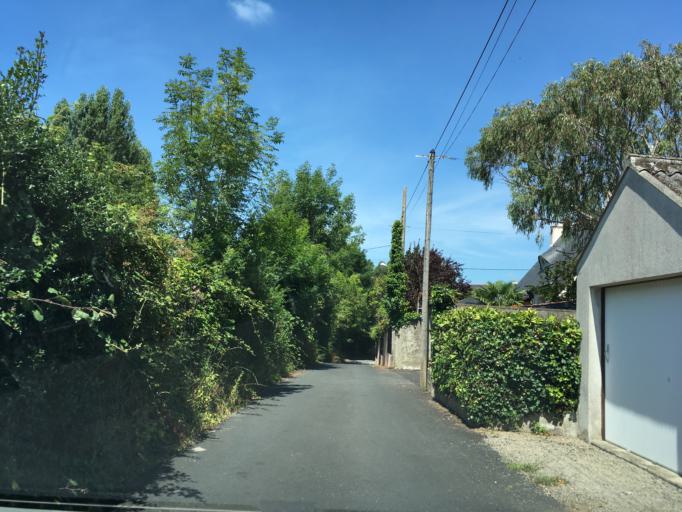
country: FR
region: Brittany
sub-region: Departement du Finistere
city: Quimper
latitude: 48.0030
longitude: -4.1058
